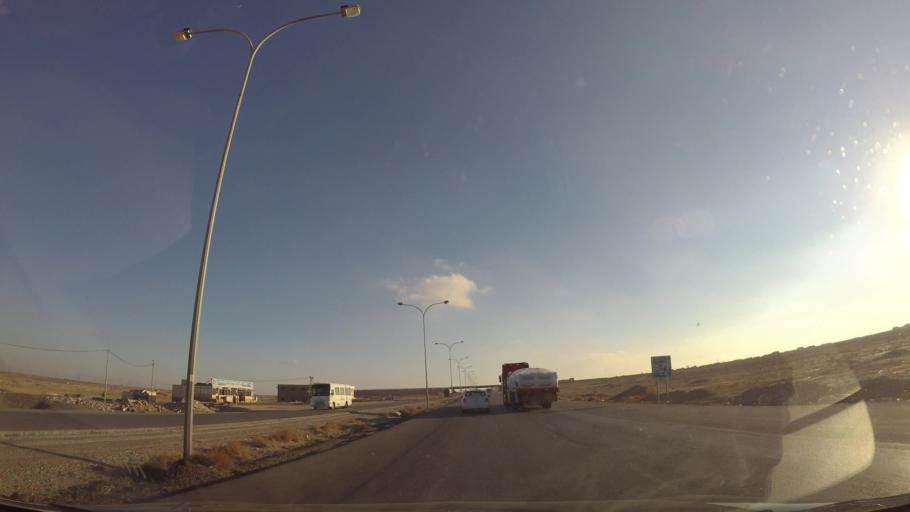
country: JO
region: Tafielah
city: Busayra
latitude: 30.5814
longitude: 35.8004
